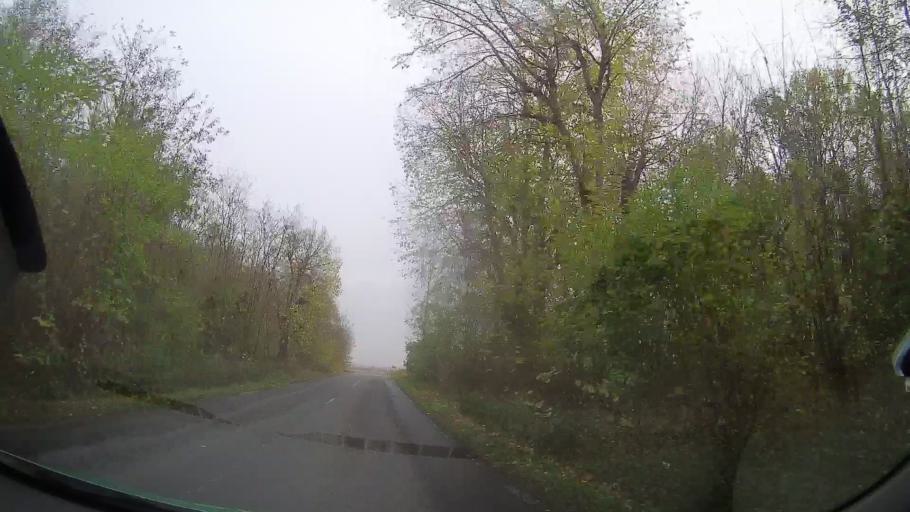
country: RO
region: Prahova
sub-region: Comuna Balta Doamnei
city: Balta Doamnei
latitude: 44.7603
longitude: 26.1340
